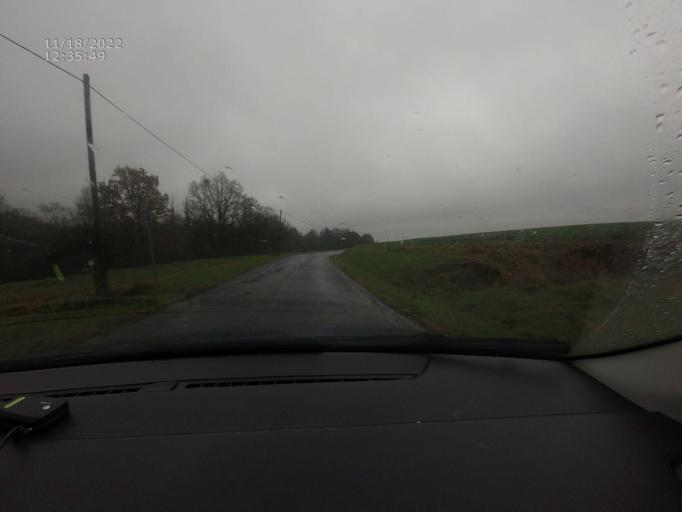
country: CZ
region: Plzensky
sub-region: Okres Klatovy
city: Planice
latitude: 49.4088
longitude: 13.5121
